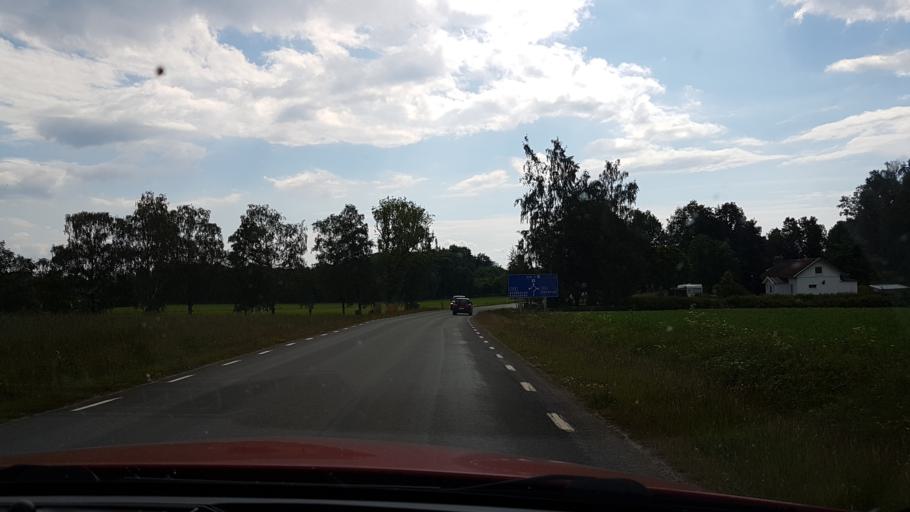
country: SE
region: Vaestra Goetaland
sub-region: Hjo Kommun
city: Hjo
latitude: 58.3057
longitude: 14.2470
